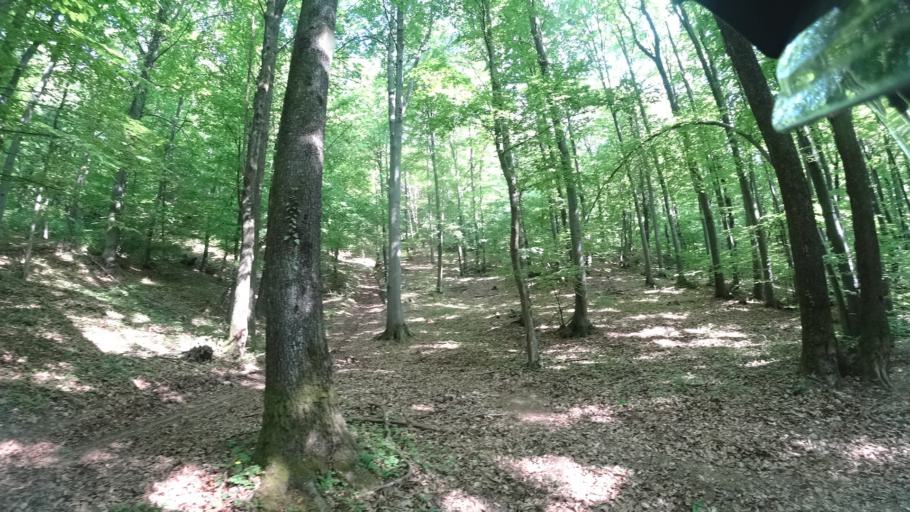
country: HR
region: Zagrebacka
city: Jablanovec
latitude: 45.8974
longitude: 15.8988
